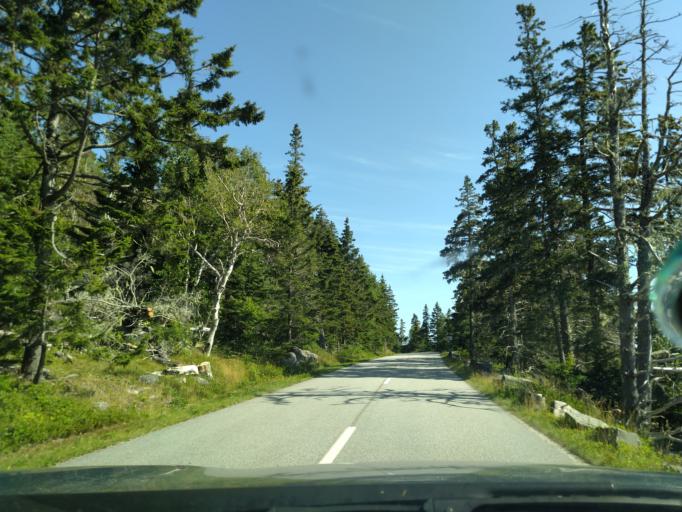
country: US
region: Maine
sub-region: Hancock County
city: Gouldsboro
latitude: 44.3408
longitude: -68.0446
